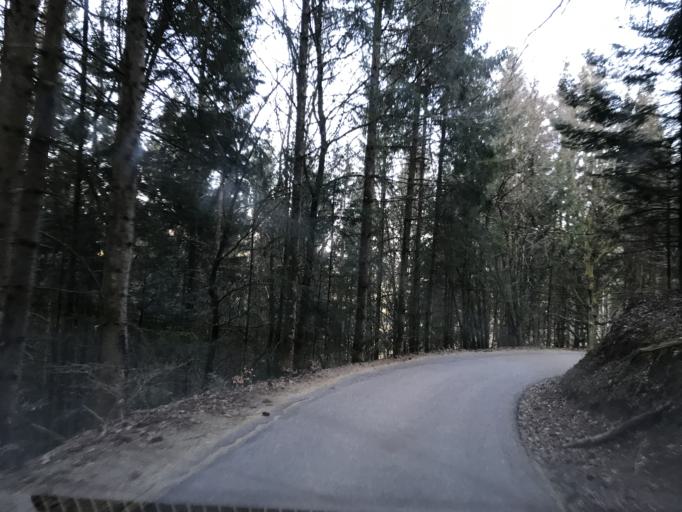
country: DE
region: Baden-Wuerttemberg
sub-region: Freiburg Region
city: Hausen
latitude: 47.6972
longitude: 7.8258
